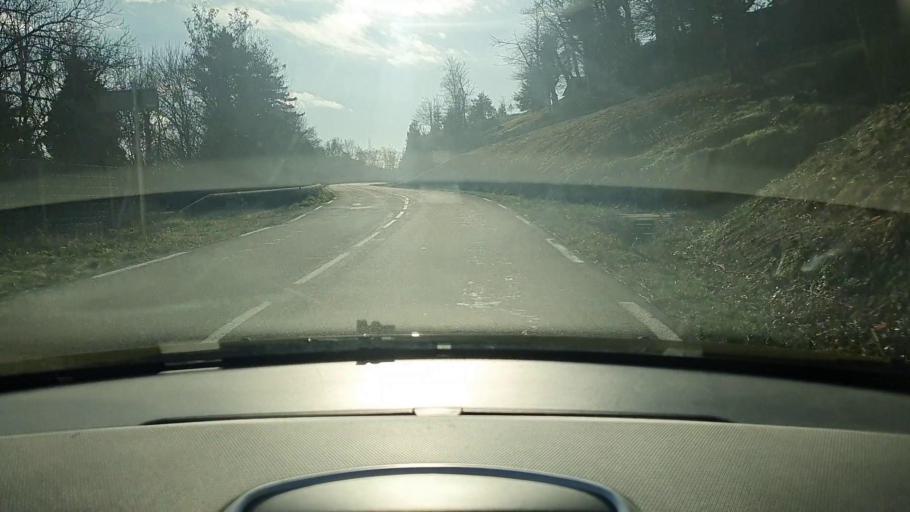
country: FR
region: Languedoc-Roussillon
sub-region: Departement du Gard
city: Branoux-les-Taillades
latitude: 44.3971
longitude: 3.9342
